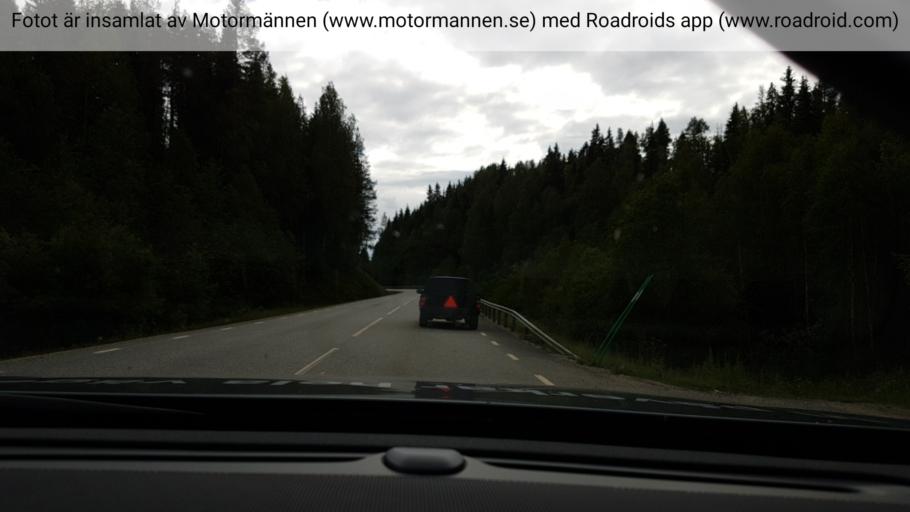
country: SE
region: Vaesterbotten
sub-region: Vindelns Kommun
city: Vindeln
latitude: 64.2044
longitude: 19.6855
